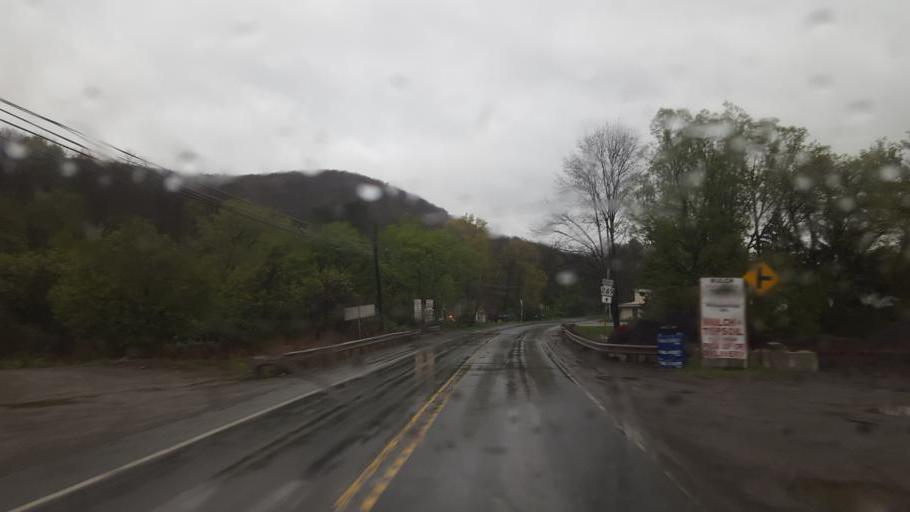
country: US
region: Pennsylvania
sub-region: Tioga County
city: Westfield
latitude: 41.9384
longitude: -77.4845
